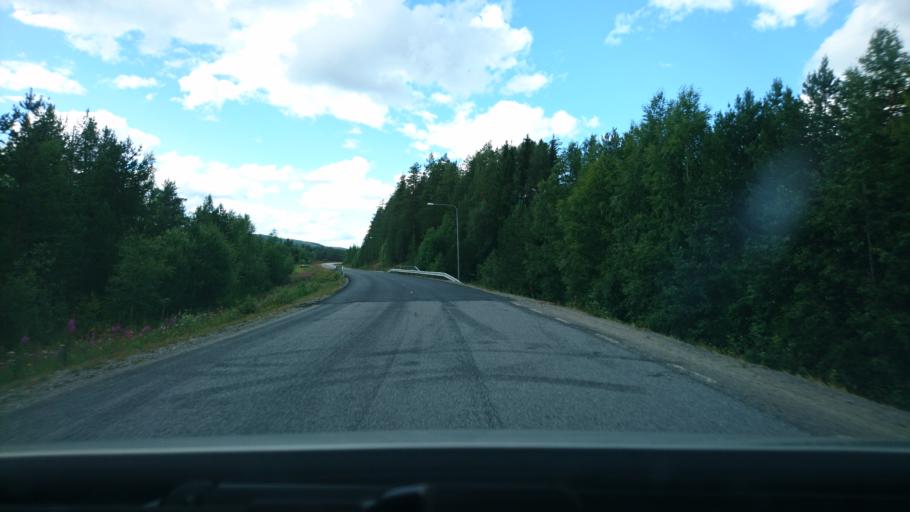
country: SE
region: Vaesterbotten
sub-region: Asele Kommun
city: Asele
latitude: 63.9431
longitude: 17.2828
